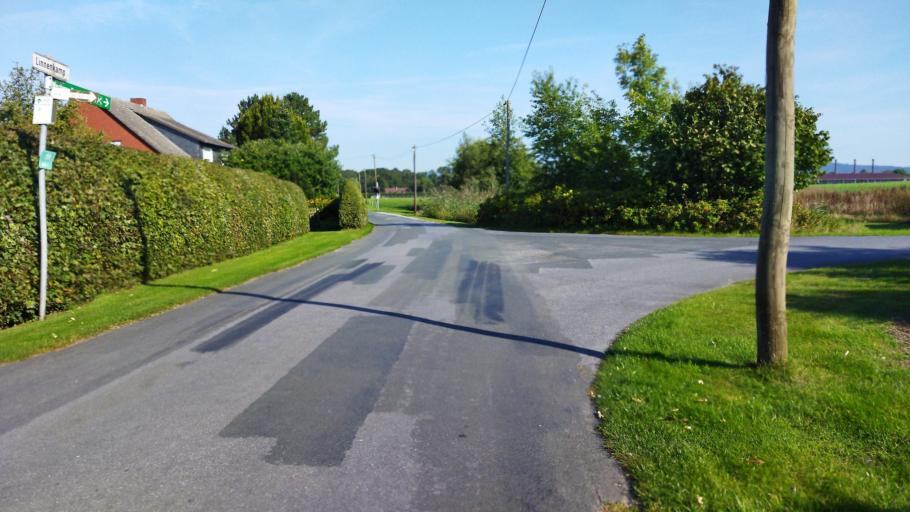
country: DE
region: Lower Saxony
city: Bad Laer
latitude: 52.1139
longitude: 8.0760
